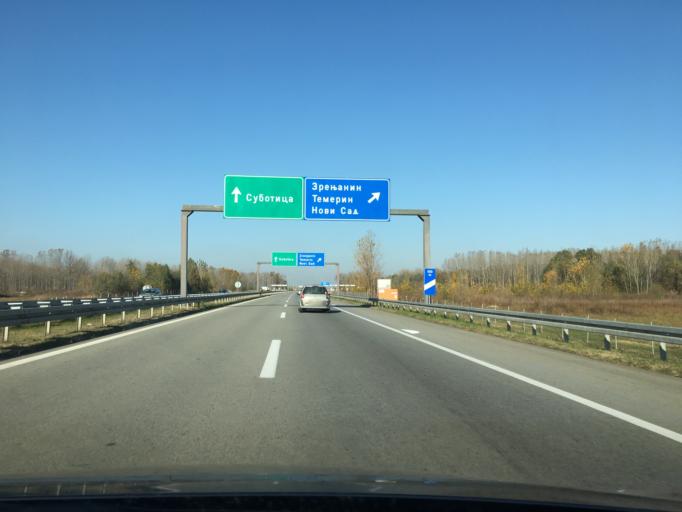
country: RS
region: Autonomna Pokrajina Vojvodina
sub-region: Juznobacki Okrug
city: Petrovaradin
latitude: 45.2846
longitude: 19.8976
